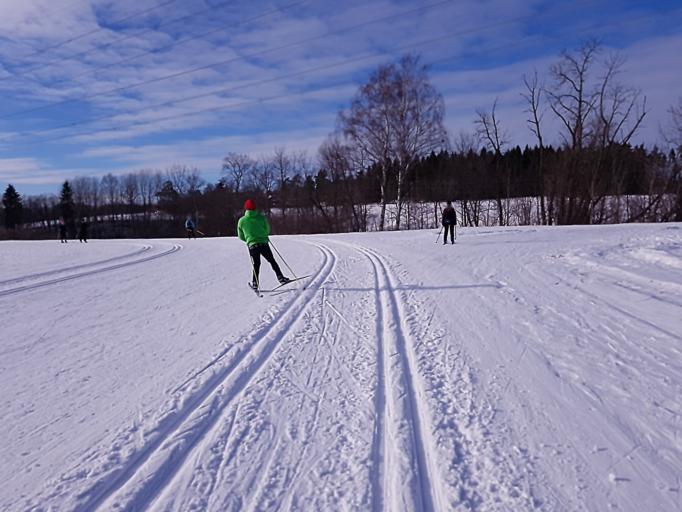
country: FI
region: Uusimaa
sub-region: Helsinki
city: Helsinki
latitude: 60.2751
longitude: 24.9365
